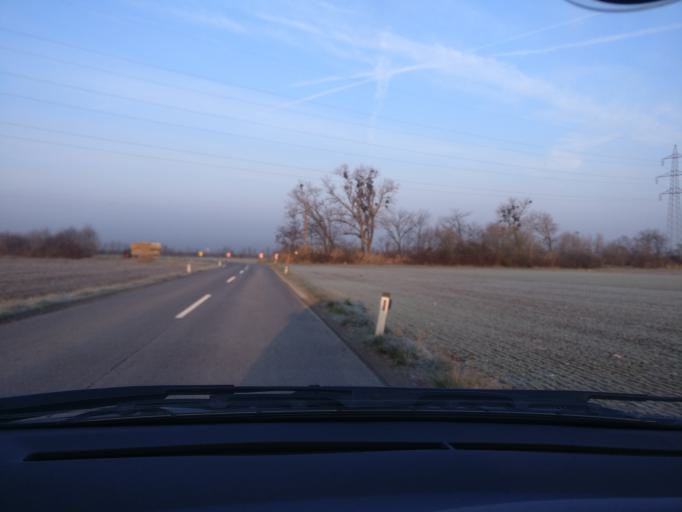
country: AT
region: Lower Austria
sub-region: Politischer Bezirk Modling
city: Munchendorf
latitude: 48.0285
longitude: 16.3709
